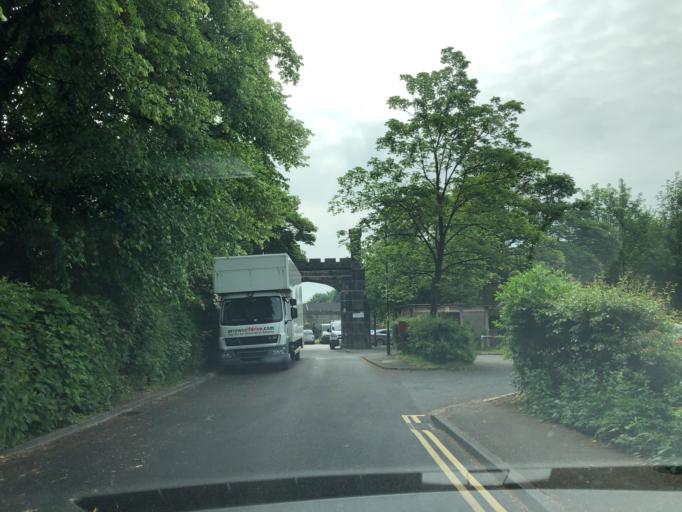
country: GB
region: England
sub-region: North Yorkshire
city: Knaresborough
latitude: 53.9977
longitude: -1.4976
